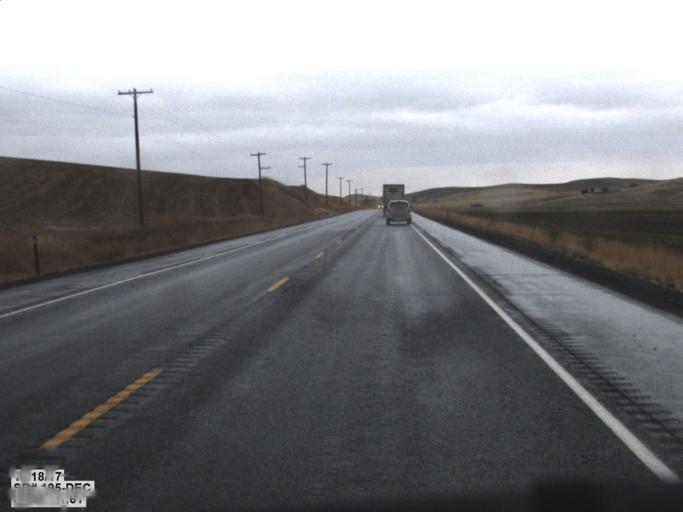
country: US
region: Washington
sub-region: Whitman County
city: Colfax
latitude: 46.8053
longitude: -117.3176
